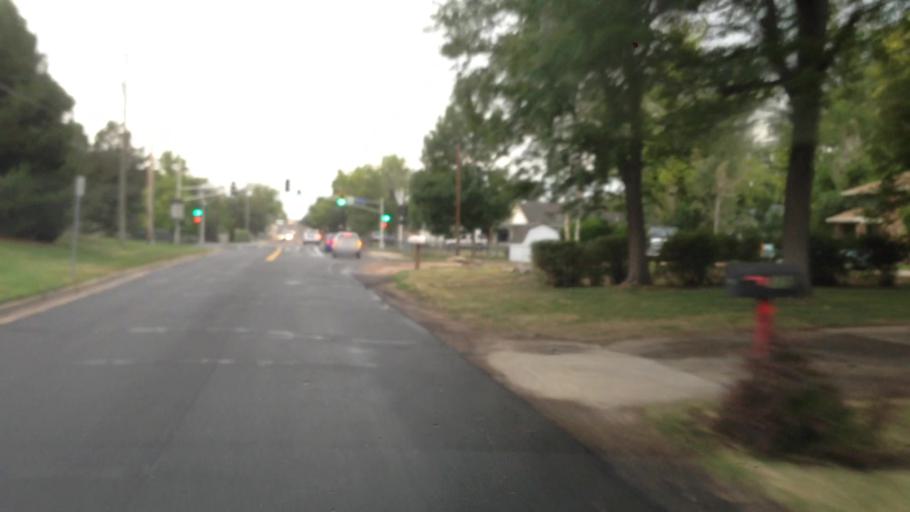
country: US
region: Colorado
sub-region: Jefferson County
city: Lakewood
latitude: 39.7194
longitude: -105.0769
